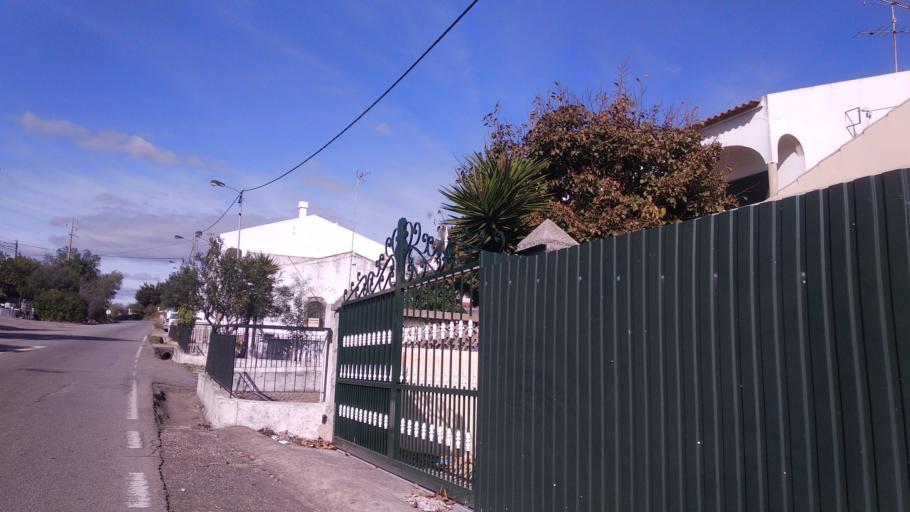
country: PT
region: Faro
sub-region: Sao Bras de Alportel
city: Sao Bras de Alportel
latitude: 37.1601
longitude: -7.8995
